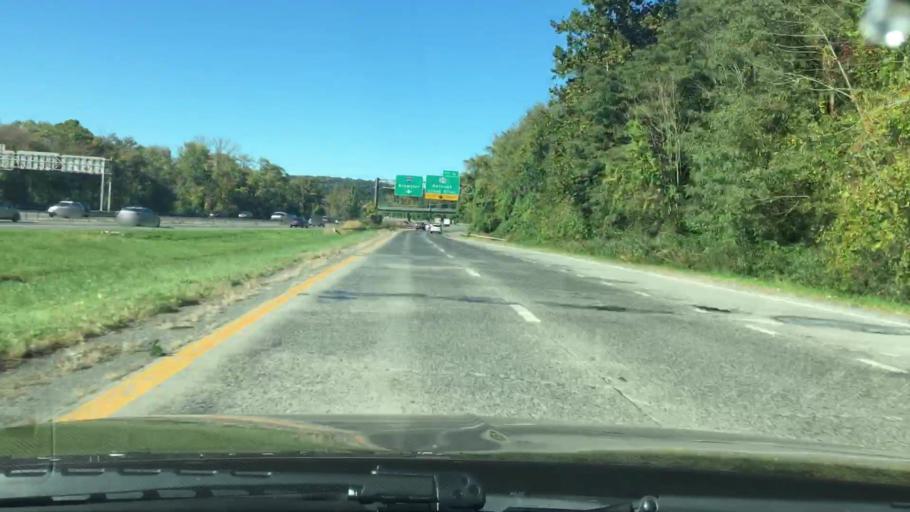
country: US
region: New York
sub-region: Westchester County
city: Katonah
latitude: 41.2560
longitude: -73.6776
